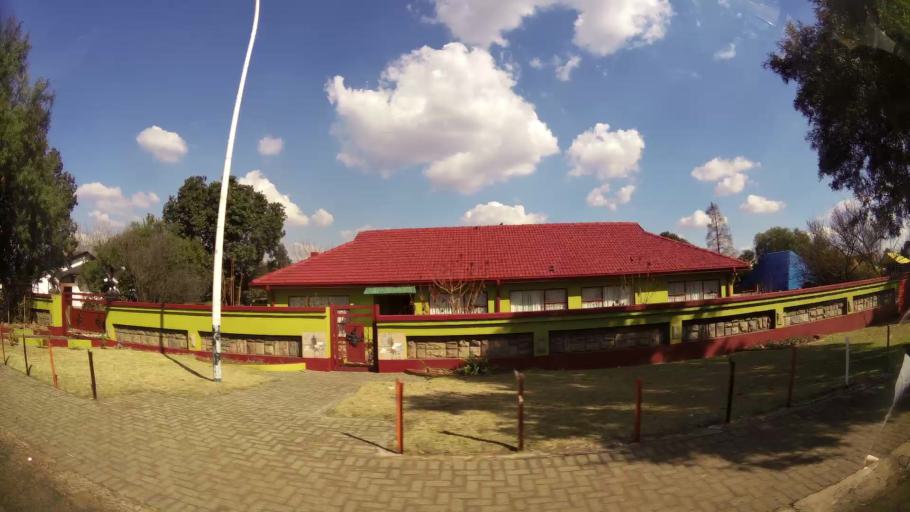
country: ZA
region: Mpumalanga
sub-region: Nkangala District Municipality
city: Witbank
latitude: -25.9263
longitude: 29.2381
